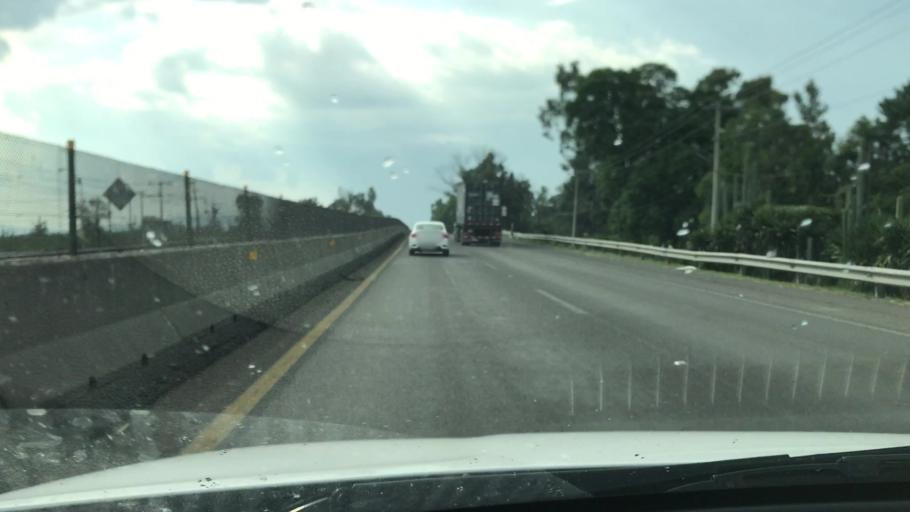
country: MX
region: Guanajuato
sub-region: Irapuato
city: Cuarta Brigada
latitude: 20.6451
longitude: -101.2892
